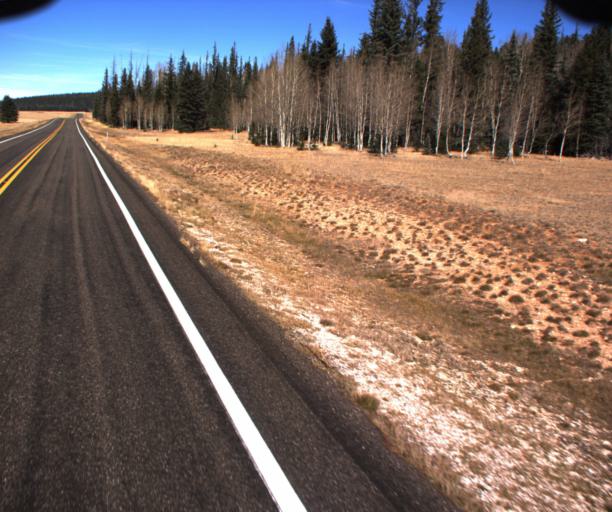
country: US
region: Arizona
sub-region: Coconino County
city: Grand Canyon
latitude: 36.3484
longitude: -112.1177
